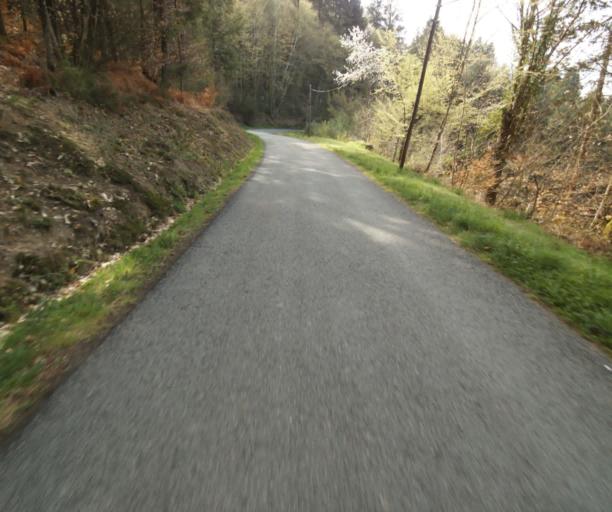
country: FR
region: Limousin
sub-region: Departement de la Correze
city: Correze
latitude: 45.3330
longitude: 1.8291
